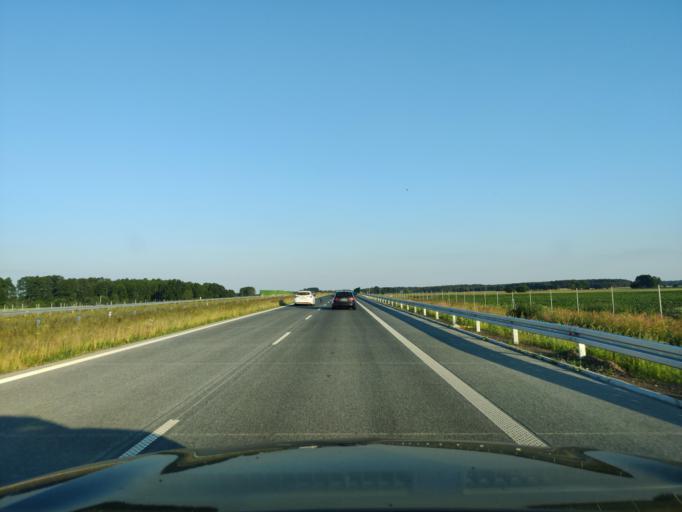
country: PL
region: Masovian Voivodeship
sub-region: Powiat mlawski
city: Strzegowo
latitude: 52.8764
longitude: 20.2744
